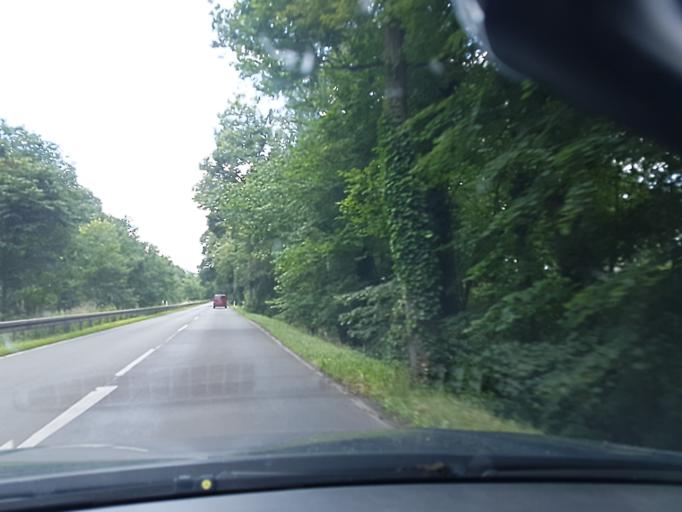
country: DE
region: Brandenburg
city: Neuruppin
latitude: 52.9245
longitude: 12.8287
